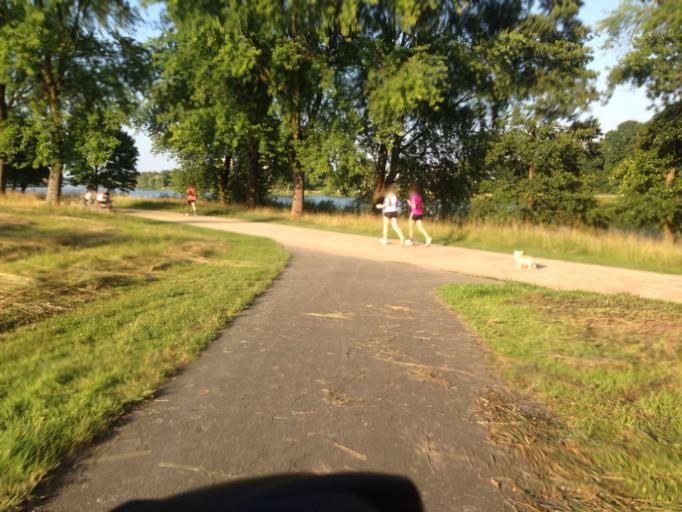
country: DE
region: North Rhine-Westphalia
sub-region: Regierungsbezirk Munster
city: Muenster
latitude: 51.9445
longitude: 7.5958
